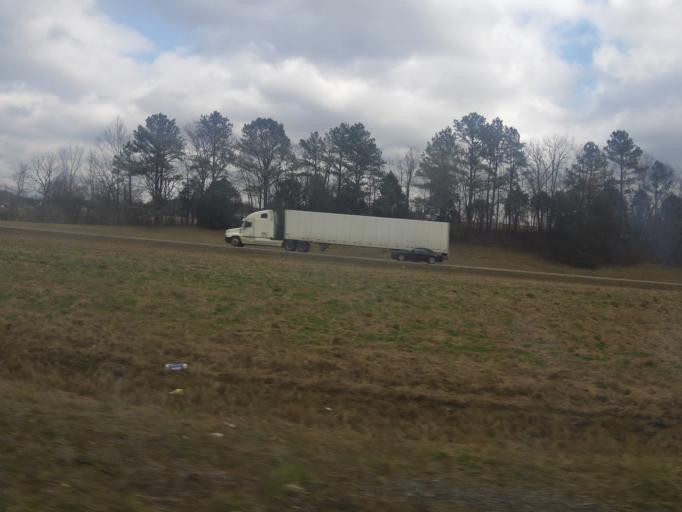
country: US
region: Tennessee
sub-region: Rutherford County
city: Plainview
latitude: 35.6181
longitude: -86.2411
